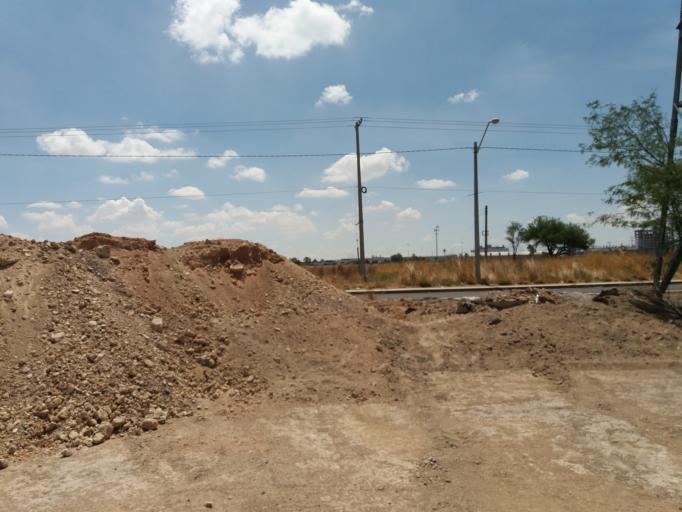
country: MX
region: Aguascalientes
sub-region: Aguascalientes
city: San Sebastian [Fraccionamiento]
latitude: 21.8132
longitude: -102.2928
